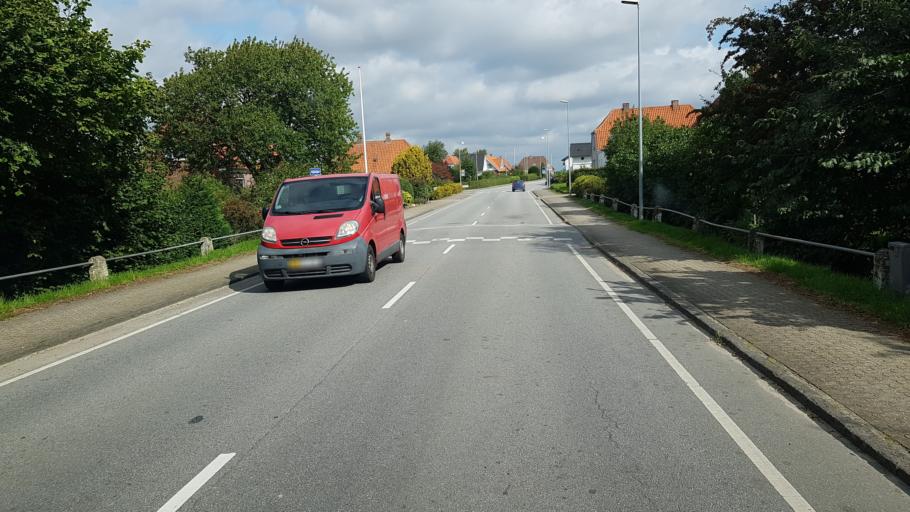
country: DK
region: South Denmark
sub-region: Kolding Kommune
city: Christiansfeld
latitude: 55.3218
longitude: 9.5624
